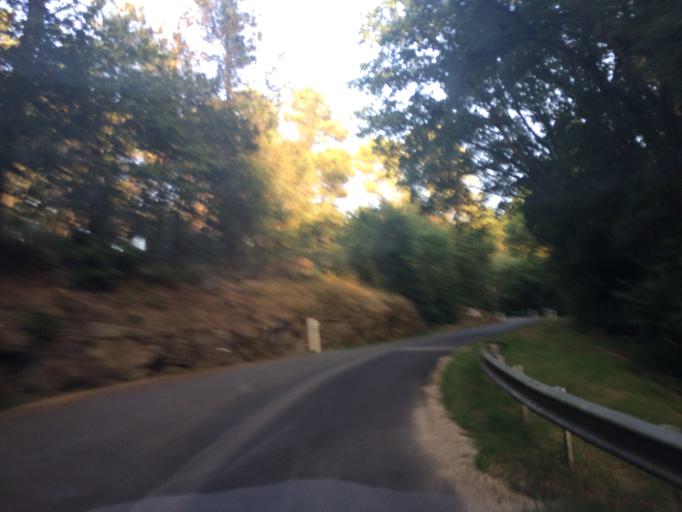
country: FR
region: Brittany
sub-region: Departement du Morbihan
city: Caden
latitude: 47.6360
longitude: -2.2537
